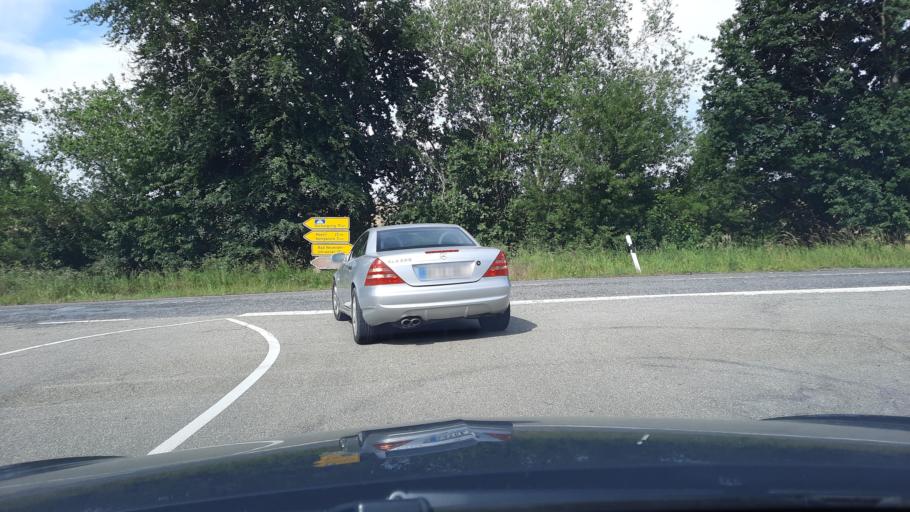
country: DE
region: Rheinland-Pfalz
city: Spessart
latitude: 50.4460
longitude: 7.1233
